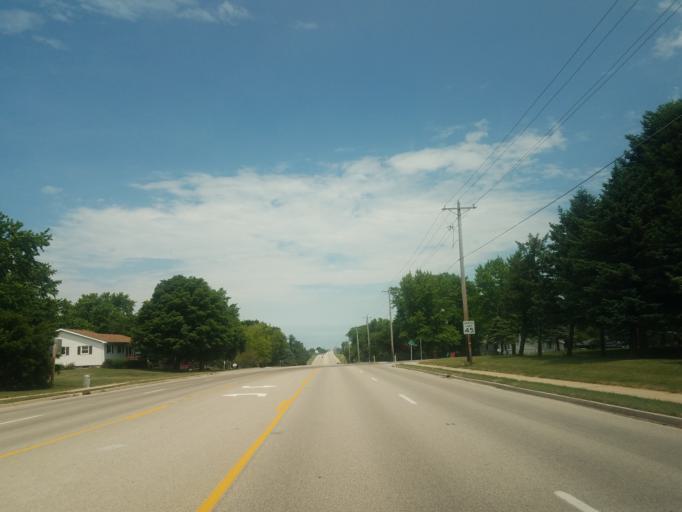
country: US
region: Illinois
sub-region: McLean County
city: Downs
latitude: 40.4223
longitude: -88.9013
